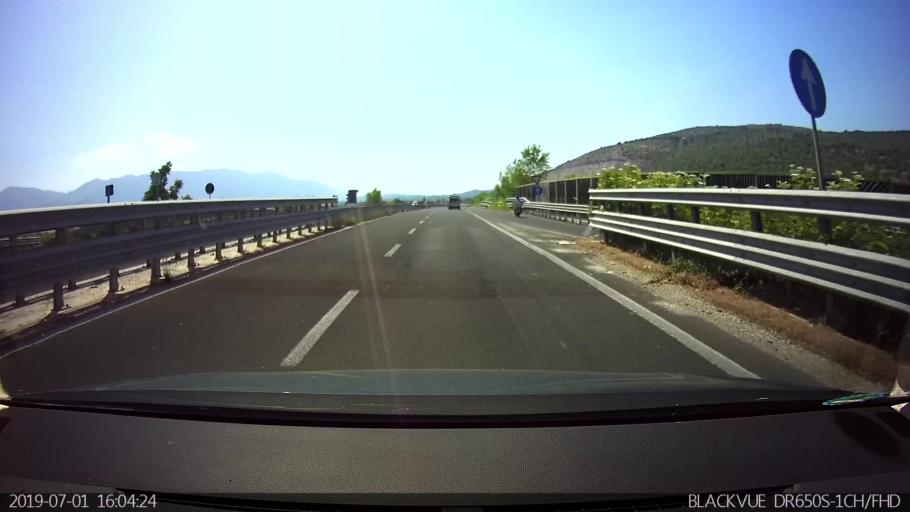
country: IT
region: Latium
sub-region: Provincia di Frosinone
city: Tecchiena
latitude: 41.6705
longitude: 13.3128
